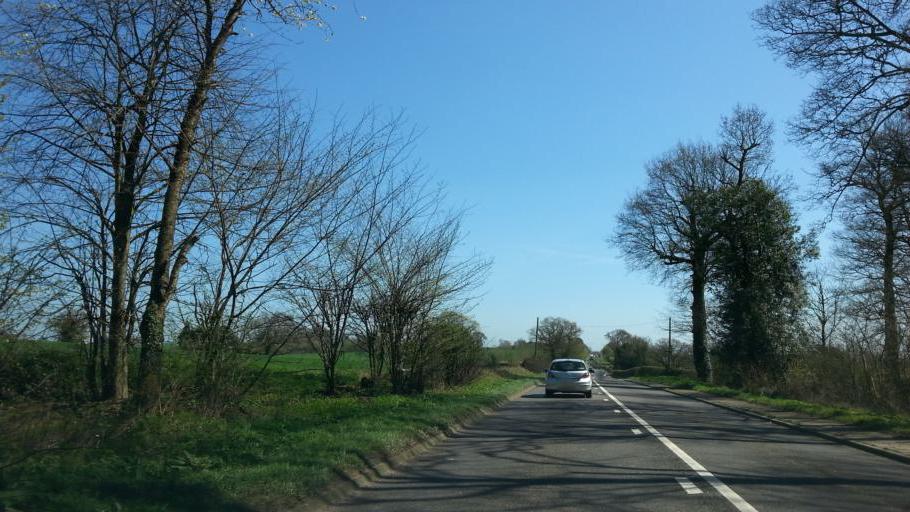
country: GB
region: England
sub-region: Staffordshire
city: Wheaton Aston
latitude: 52.6941
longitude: -2.2605
